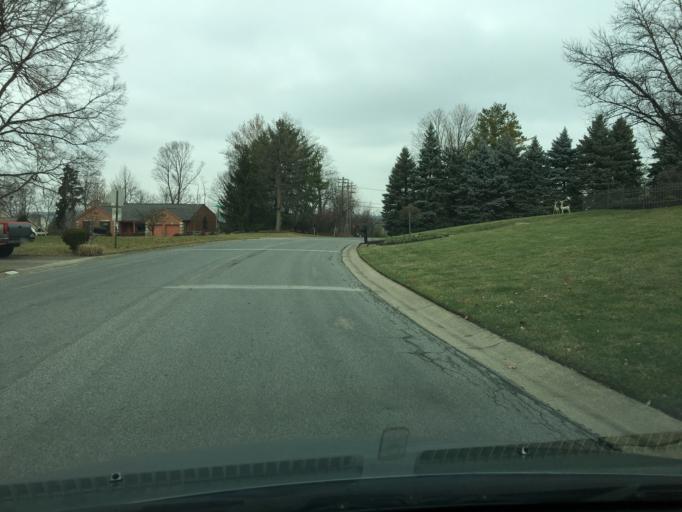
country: US
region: Ohio
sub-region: Hamilton County
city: Sharonville
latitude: 39.3115
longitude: -84.3995
